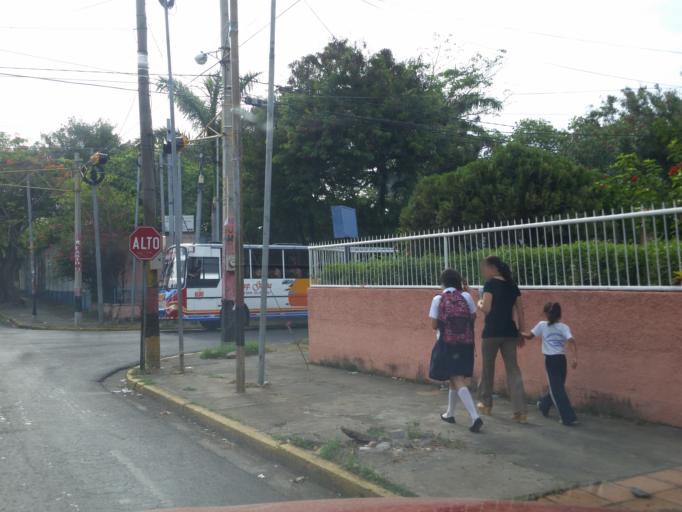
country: NI
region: Managua
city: Managua
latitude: 12.1386
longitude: -86.2656
